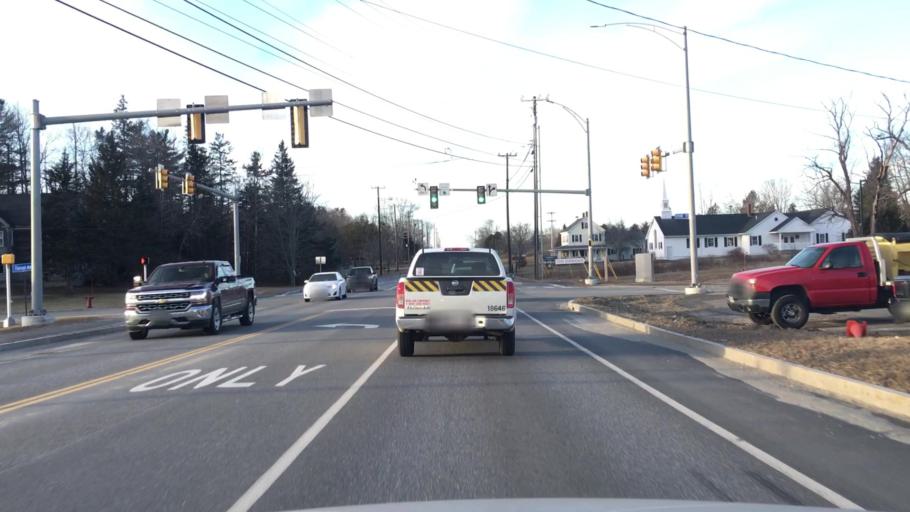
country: US
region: Maine
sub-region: Hancock County
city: Ellsworth
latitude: 44.5527
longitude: -68.4293
